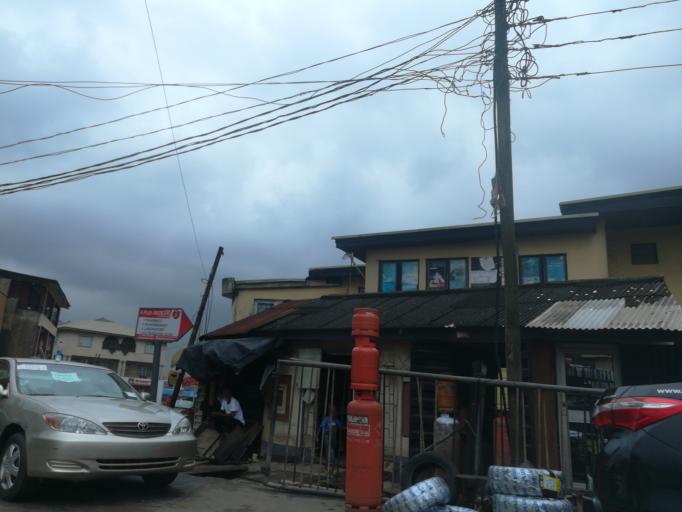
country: NG
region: Lagos
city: Ojota
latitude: 6.5713
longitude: 3.3723
